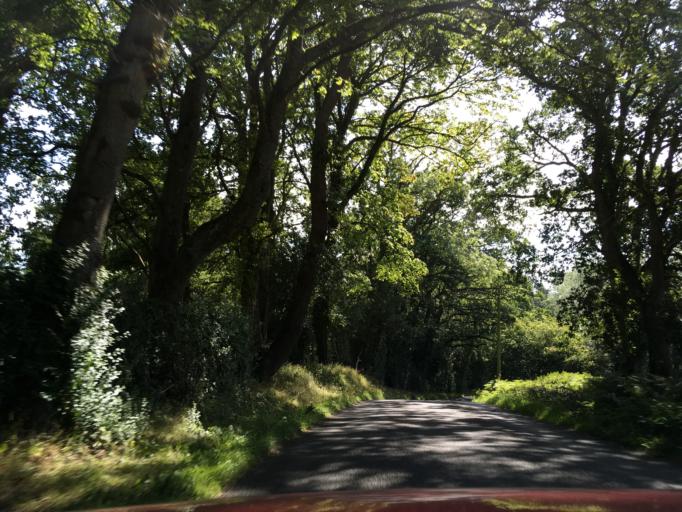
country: GB
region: England
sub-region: West Berkshire
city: Kintbury
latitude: 51.3701
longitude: -1.4326
